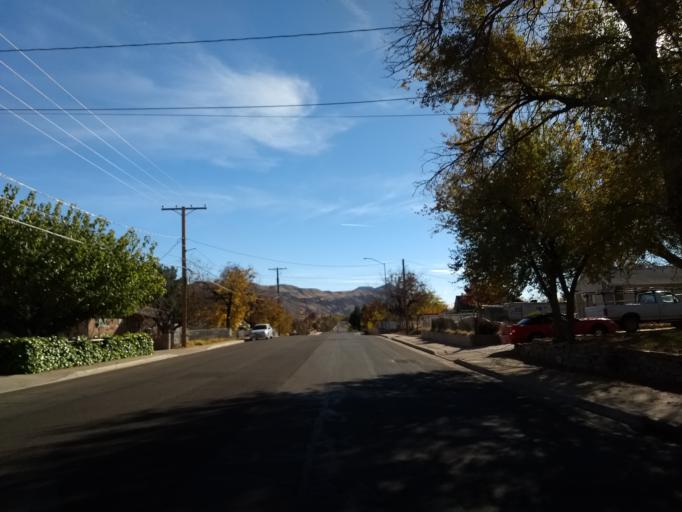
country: US
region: Utah
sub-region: Washington County
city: Hurricane
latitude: 37.1819
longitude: -113.2919
